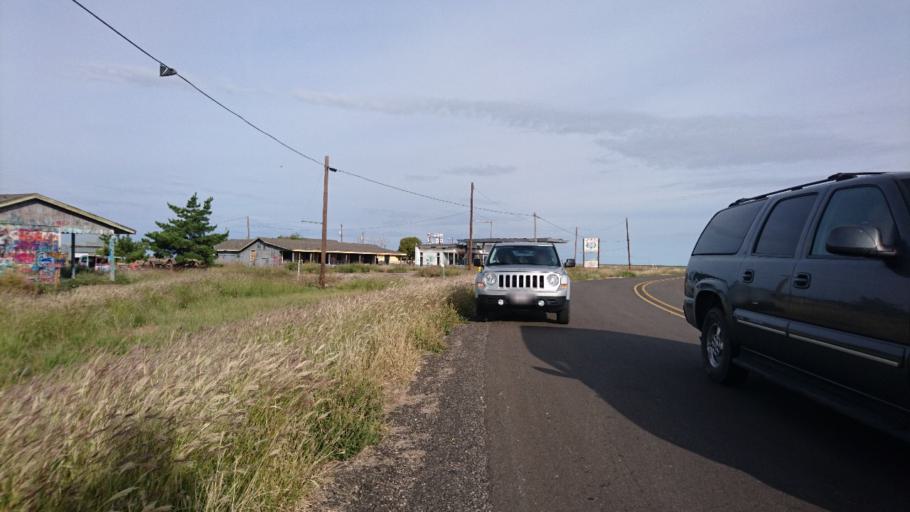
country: US
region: Texas
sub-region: Armstrong County
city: Claude
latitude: 35.2155
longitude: -101.3835
